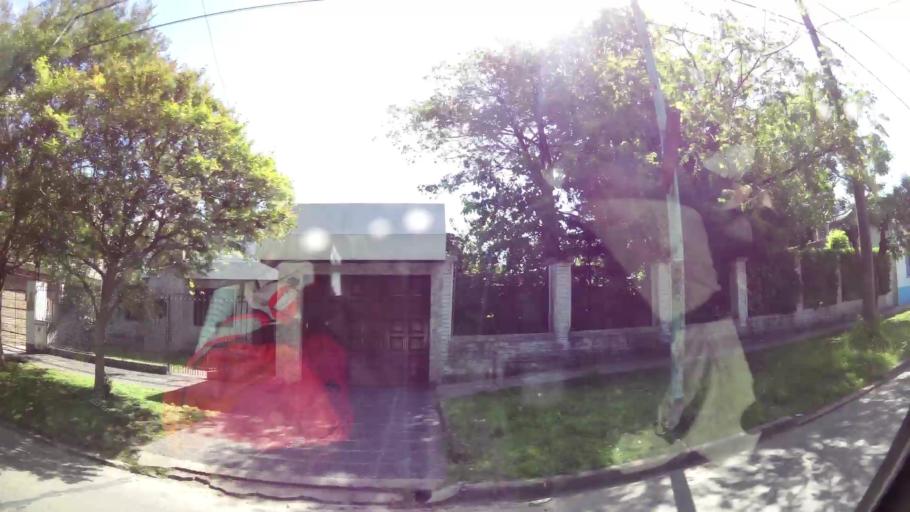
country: AR
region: Buenos Aires
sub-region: Partido de Quilmes
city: Quilmes
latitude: -34.8061
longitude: -58.2716
